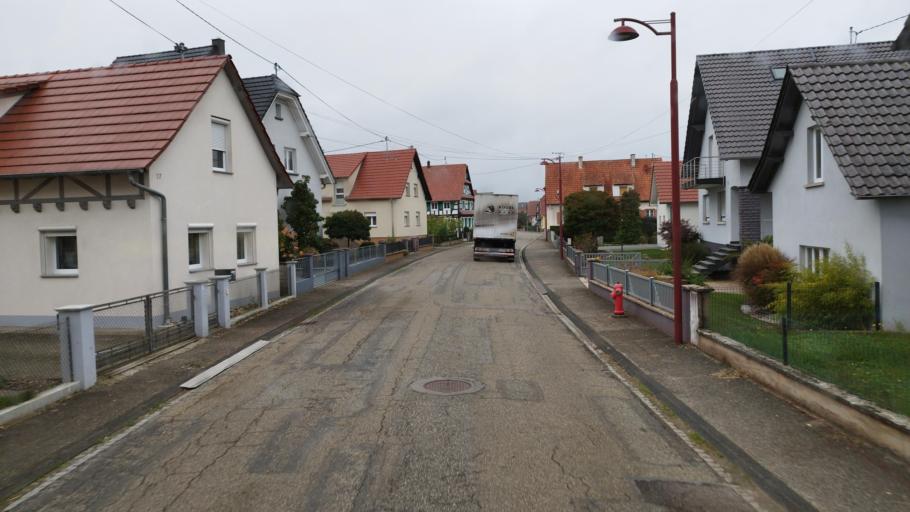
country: DE
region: Rheinland-Pfalz
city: Kapsweyer
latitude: 48.9929
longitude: 8.0238
